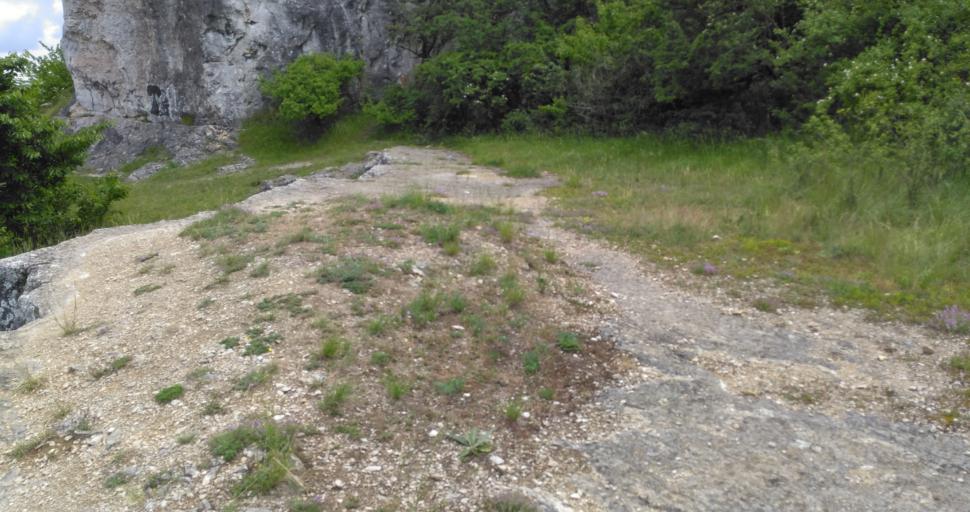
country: CZ
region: South Moravian
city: Podoli
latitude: 49.1907
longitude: 16.6752
